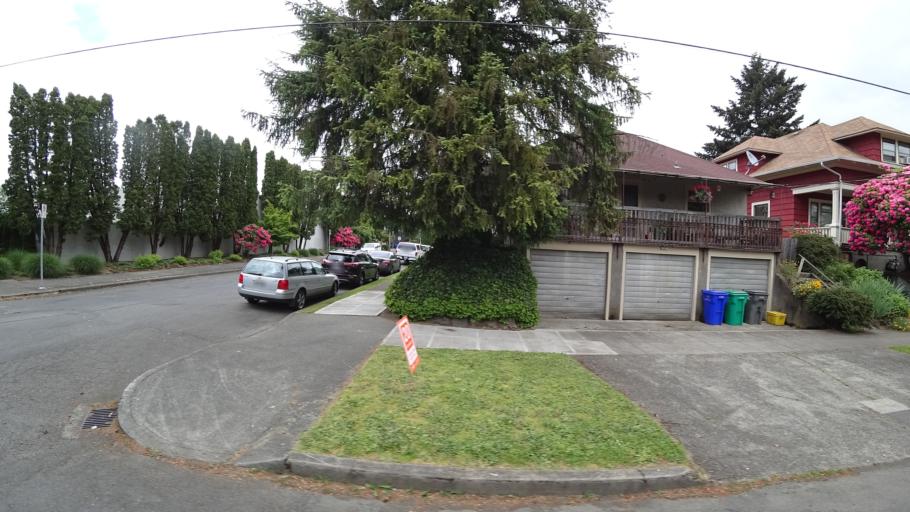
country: US
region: Oregon
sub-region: Multnomah County
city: Portland
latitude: 45.5159
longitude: -122.6210
